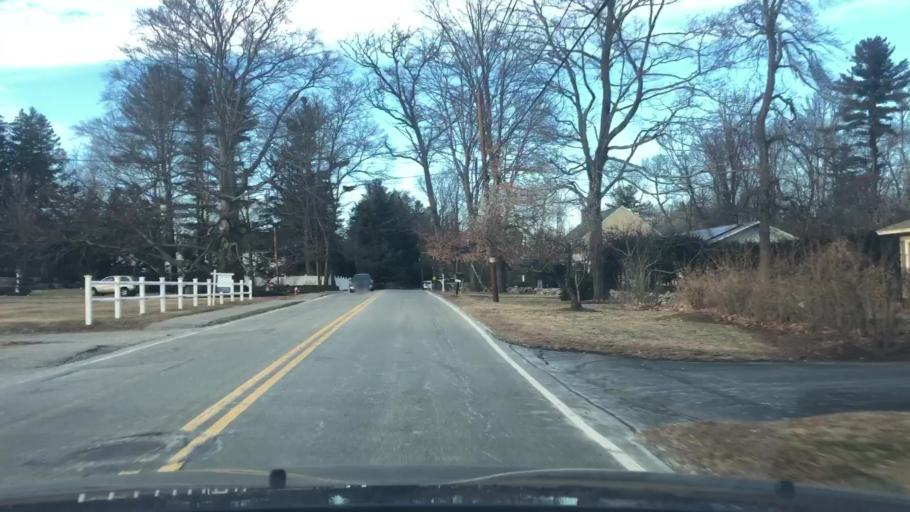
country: US
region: Massachusetts
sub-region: Essex County
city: Andover
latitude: 42.6733
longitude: -71.1138
